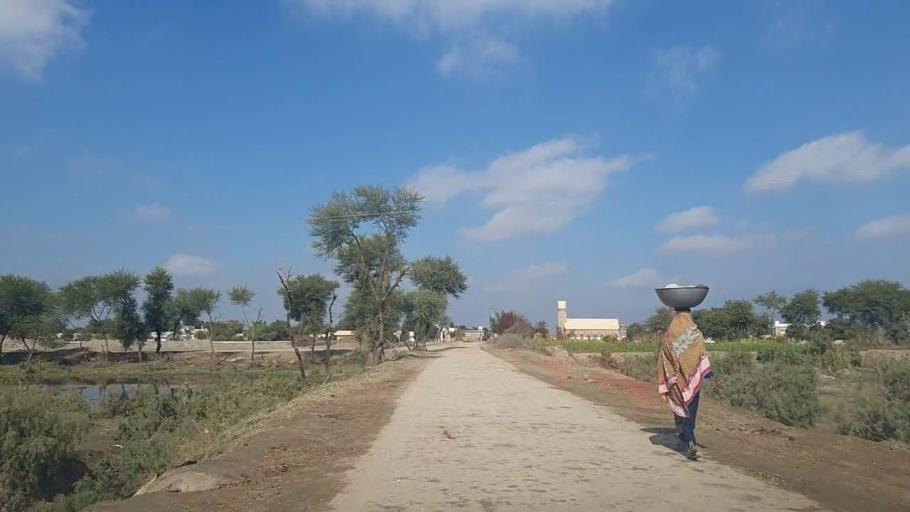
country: PK
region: Sindh
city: Sanghar
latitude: 26.0679
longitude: 68.9911
